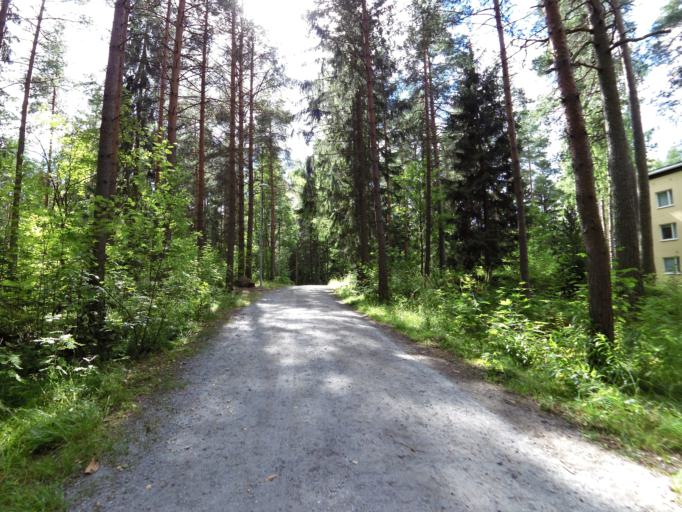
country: FI
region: Pirkanmaa
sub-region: Tampere
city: Yloejaervi
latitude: 61.5081
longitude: 23.6088
